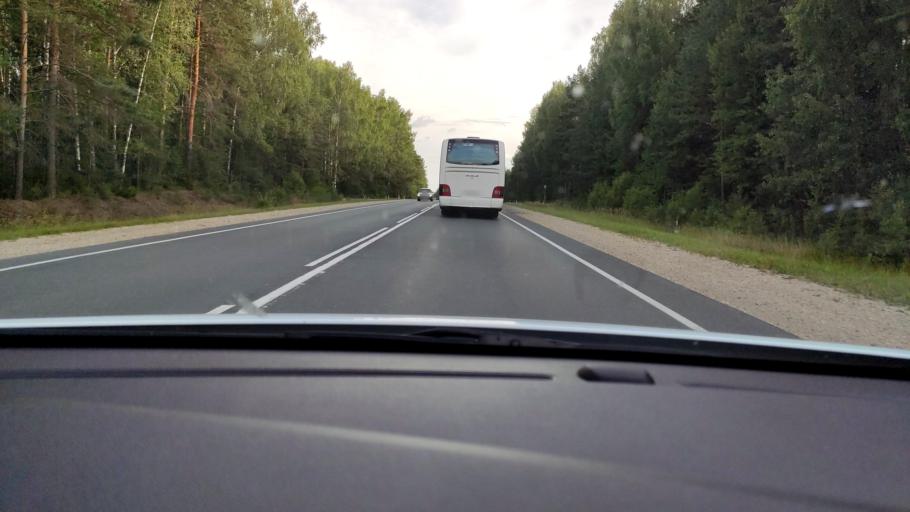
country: RU
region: Mariy-El
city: Suslonger
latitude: 56.2974
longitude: 48.2339
